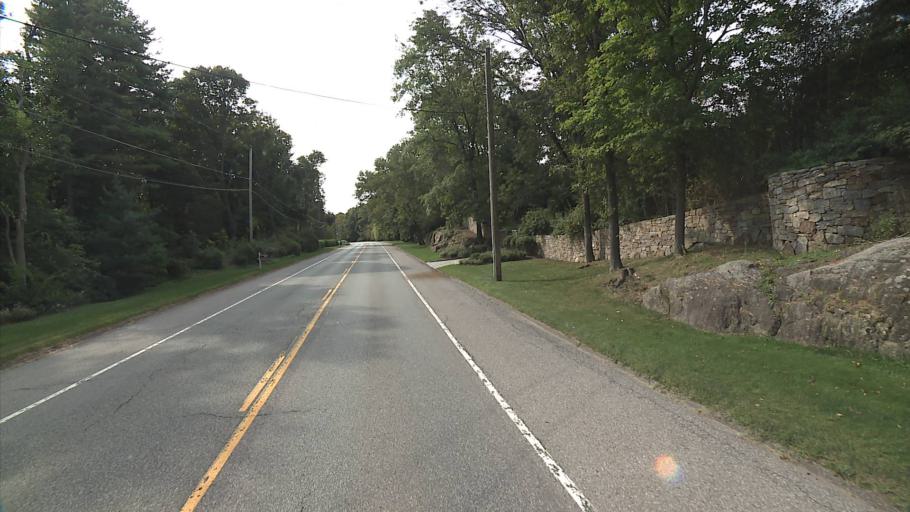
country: US
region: Connecticut
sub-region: Fairfield County
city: New Canaan
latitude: 41.1891
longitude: -73.5057
